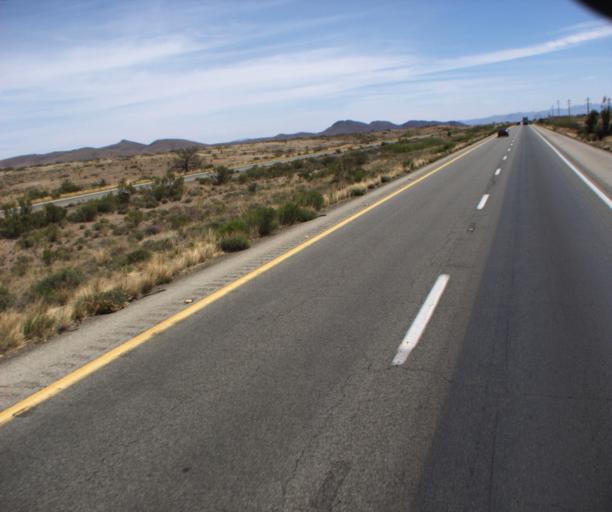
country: US
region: Arizona
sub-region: Cochise County
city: Willcox
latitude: 32.3600
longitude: -109.6699
